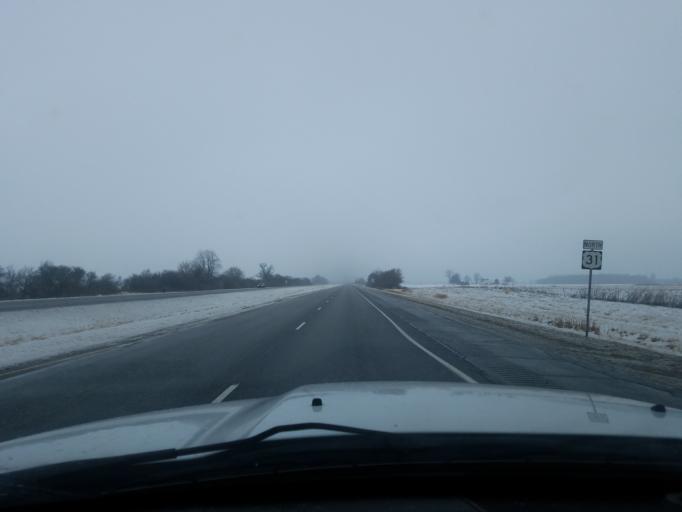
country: US
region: Indiana
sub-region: Fulton County
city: Rochester
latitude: 40.9827
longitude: -86.1679
